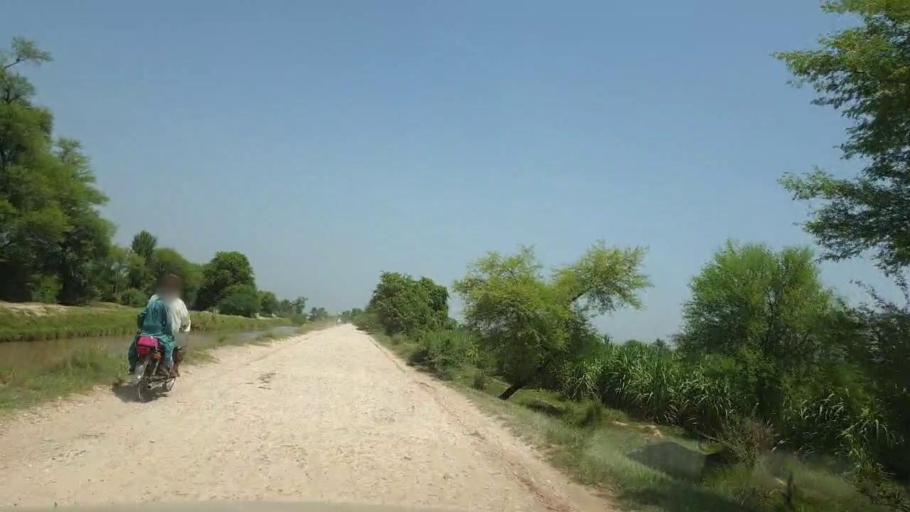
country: PK
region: Sindh
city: Pano Aqil
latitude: 27.6579
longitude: 69.1070
